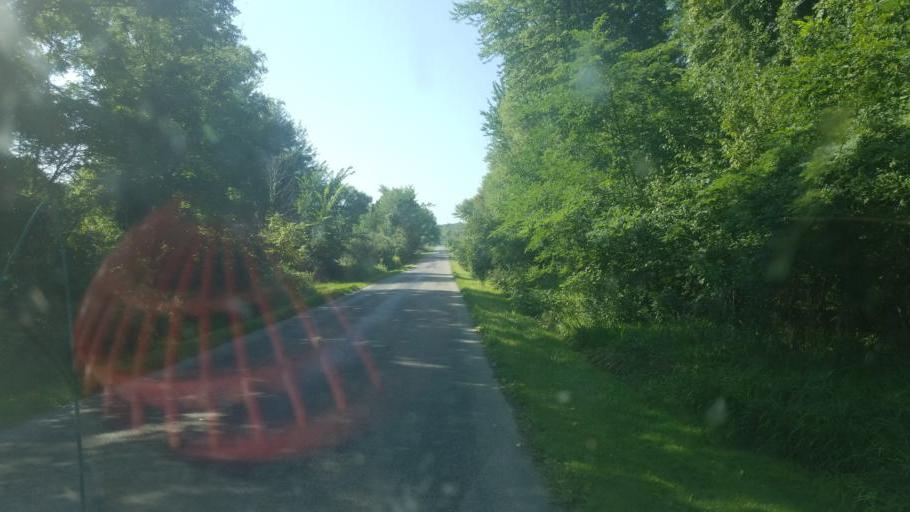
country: US
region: Ohio
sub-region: Lorain County
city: Wellington
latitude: 41.0722
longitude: -82.2015
